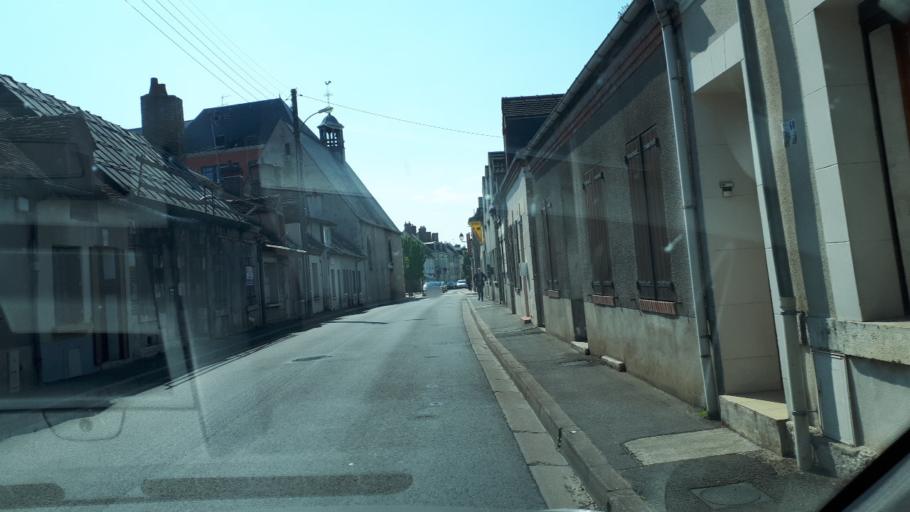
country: FR
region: Centre
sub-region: Departement du Loir-et-Cher
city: Romorantin-Lanthenay
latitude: 47.3638
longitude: 1.7419
